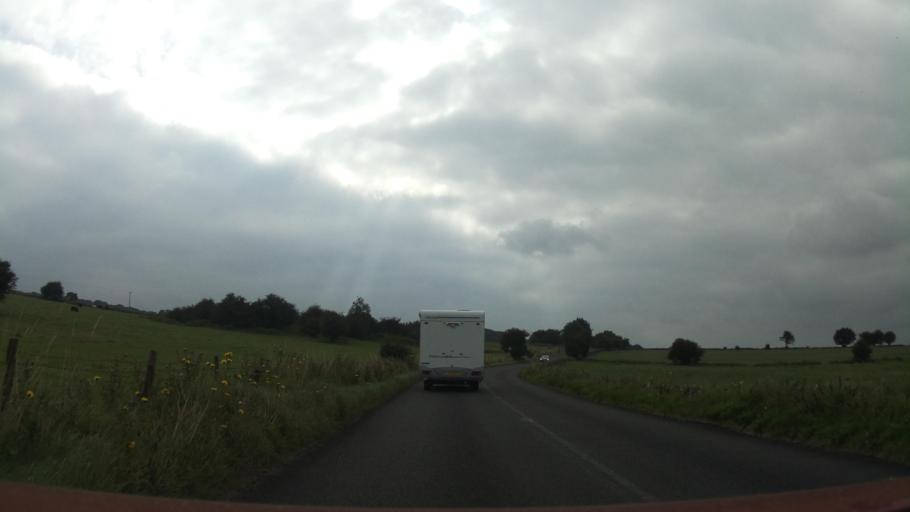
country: GB
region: England
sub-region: Staffordshire
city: Mayfield
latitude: 53.0258
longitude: -1.8404
